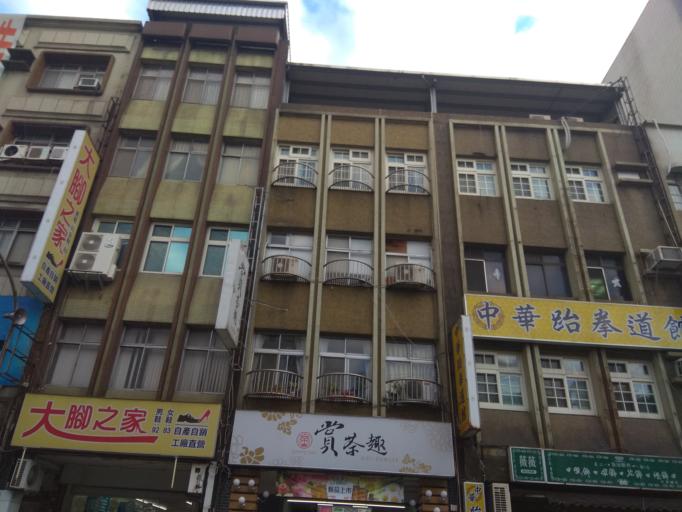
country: TW
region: Taiwan
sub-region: Taoyuan
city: Taoyuan
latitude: 24.9904
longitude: 121.3096
